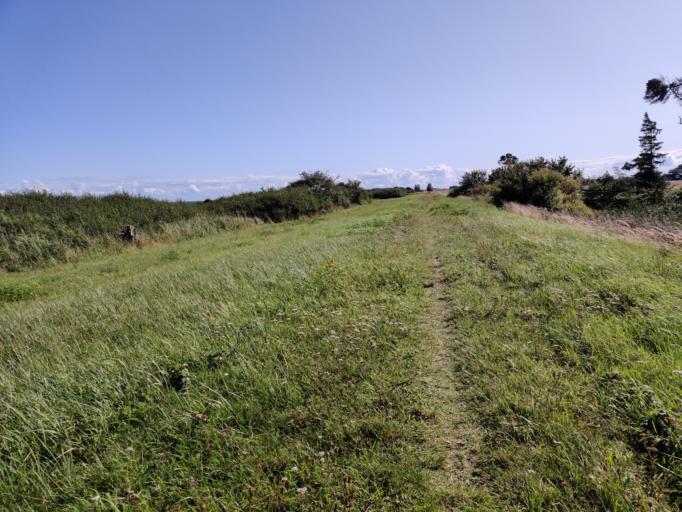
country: DK
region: Zealand
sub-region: Guldborgsund Kommune
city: Nykobing Falster
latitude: 54.5780
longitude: 11.9723
